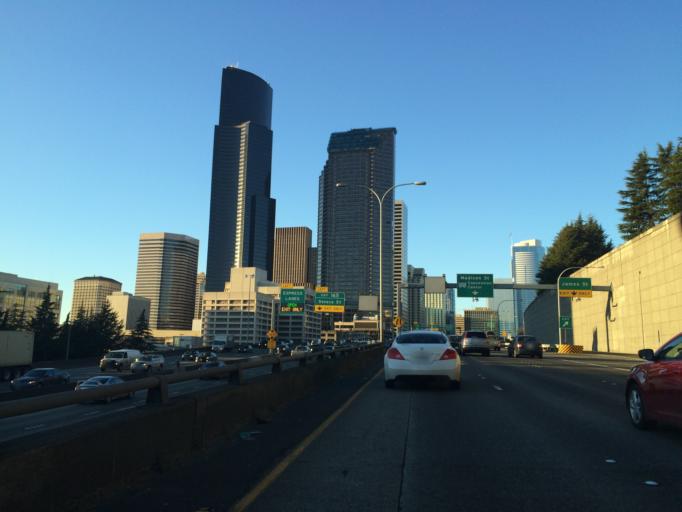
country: US
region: Washington
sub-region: King County
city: Seattle
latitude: 47.6021
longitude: -122.3248
